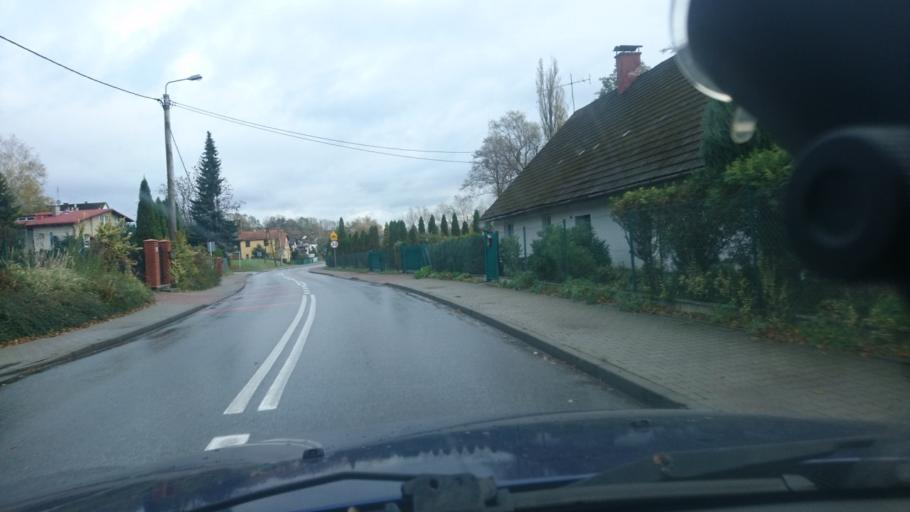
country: PL
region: Silesian Voivodeship
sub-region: Bielsko-Biala
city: Bielsko-Biala
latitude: 49.8277
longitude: 19.0208
